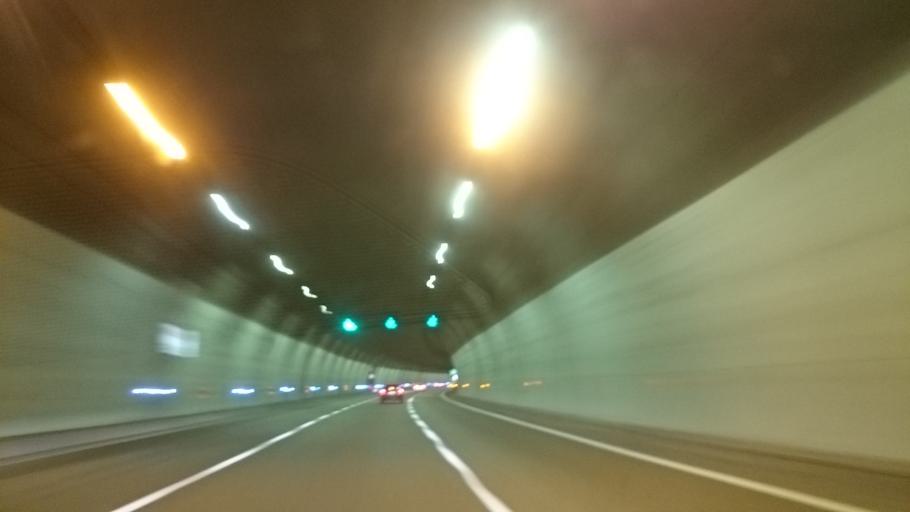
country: IT
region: Emilia-Romagna
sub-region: Provincia di Bologna
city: Vado
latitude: 44.3137
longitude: 11.2511
